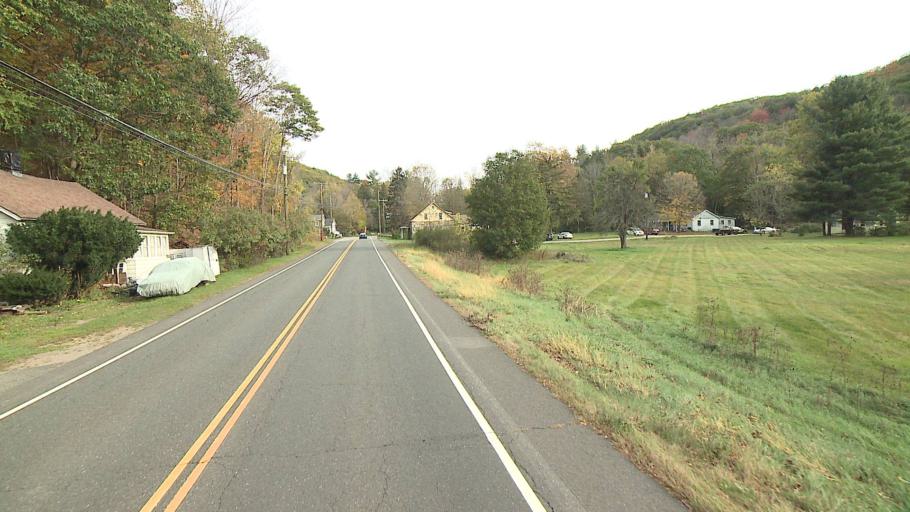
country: US
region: Connecticut
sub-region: Litchfield County
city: Canaan
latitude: 42.0053
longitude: -73.2276
